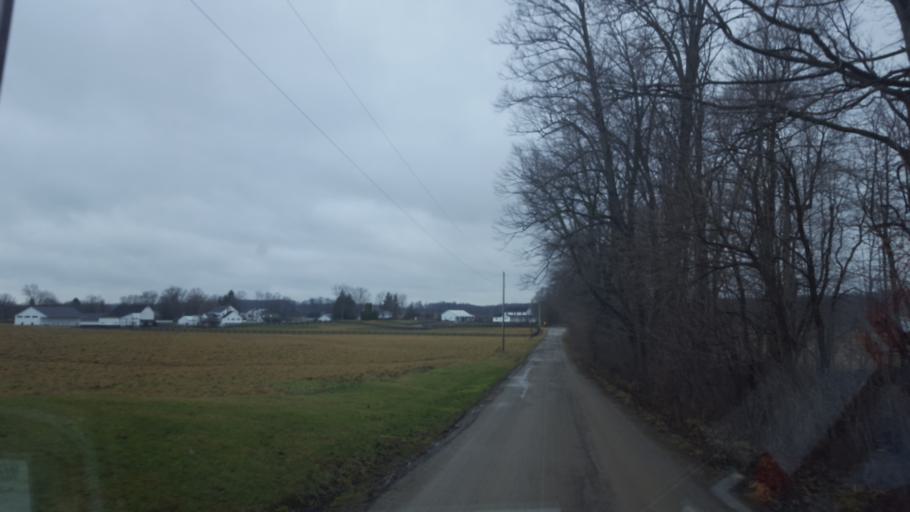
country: US
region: Ohio
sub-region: Knox County
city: Fredericktown
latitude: 40.5379
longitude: -82.6141
